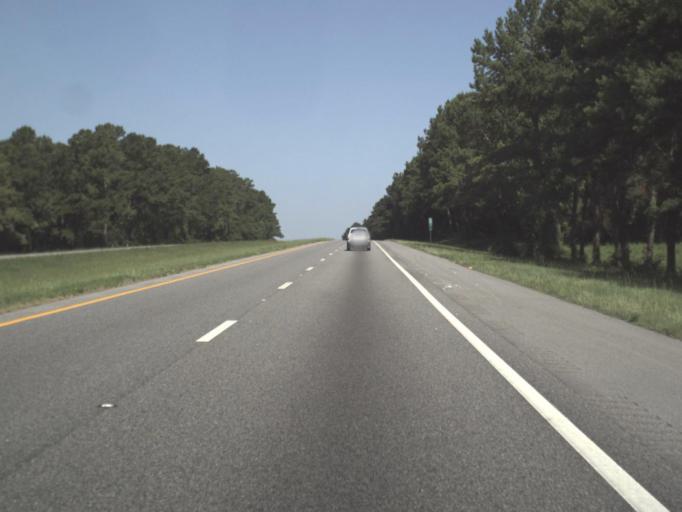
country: US
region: Florida
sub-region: Suwannee County
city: Live Oak
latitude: 30.3462
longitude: -82.9861
